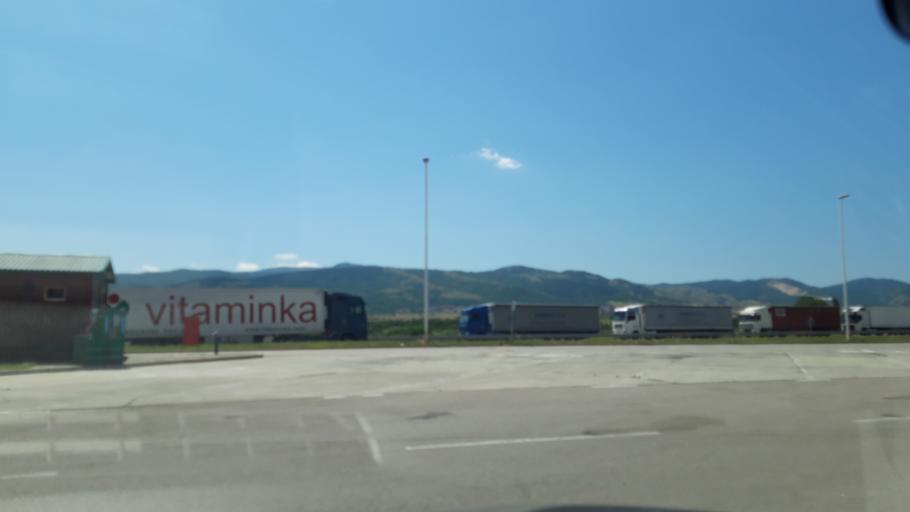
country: MK
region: Opstina Lipkovo
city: Lojane
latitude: 42.2452
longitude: 21.7027
